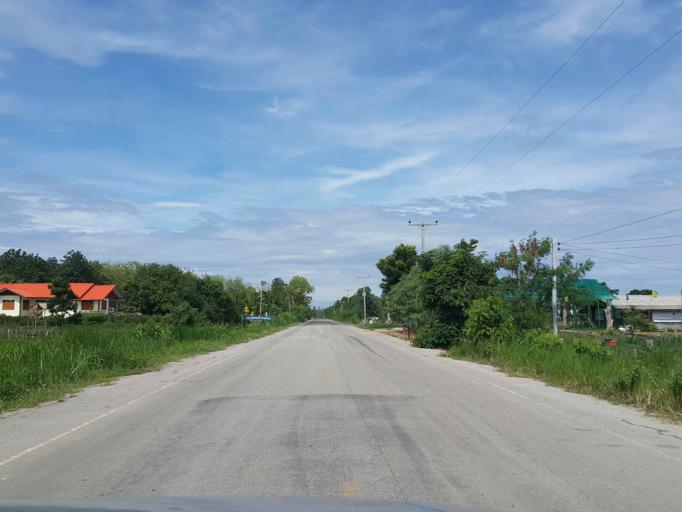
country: TH
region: Sukhothai
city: Ban Dan Lan Hoi
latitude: 17.1149
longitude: 99.5173
